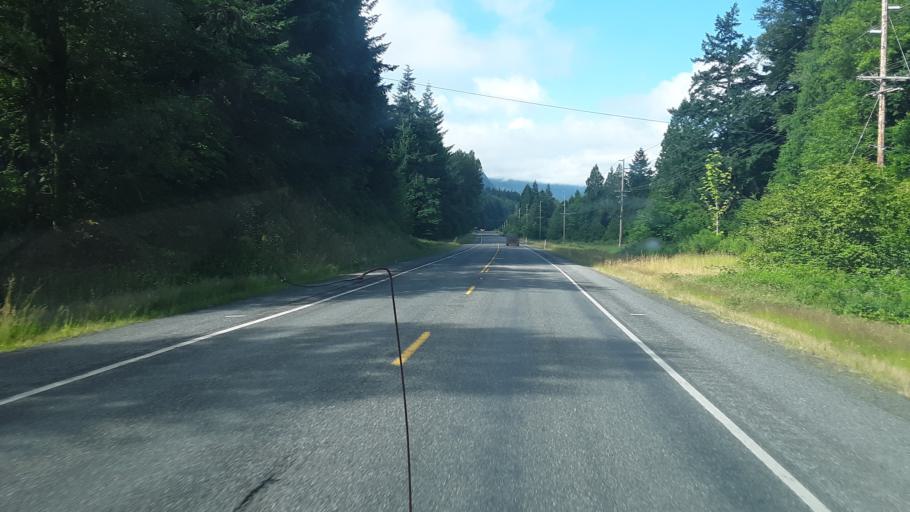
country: US
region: Washington
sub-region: Lewis County
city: Morton
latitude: 46.5470
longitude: -121.7453
